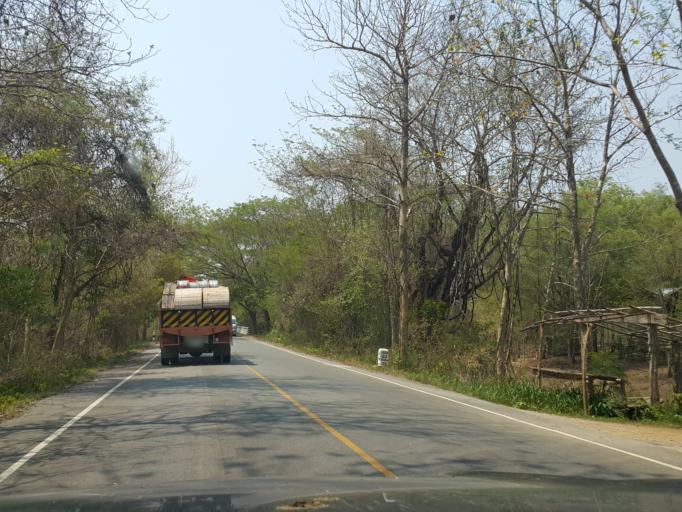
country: TH
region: Sukhothai
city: Thung Saliam
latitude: 17.3854
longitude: 99.3989
